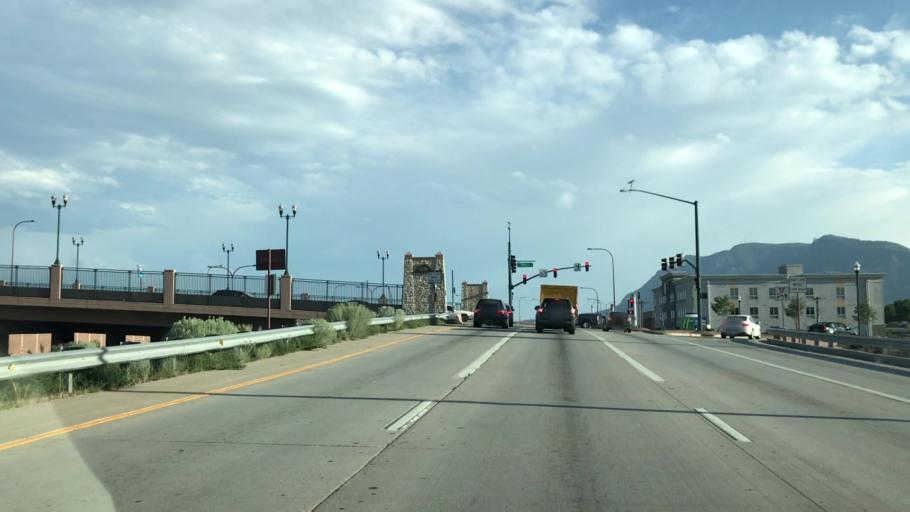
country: US
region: Colorado
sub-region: El Paso County
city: Colorado Springs
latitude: 38.8377
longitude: -104.8307
